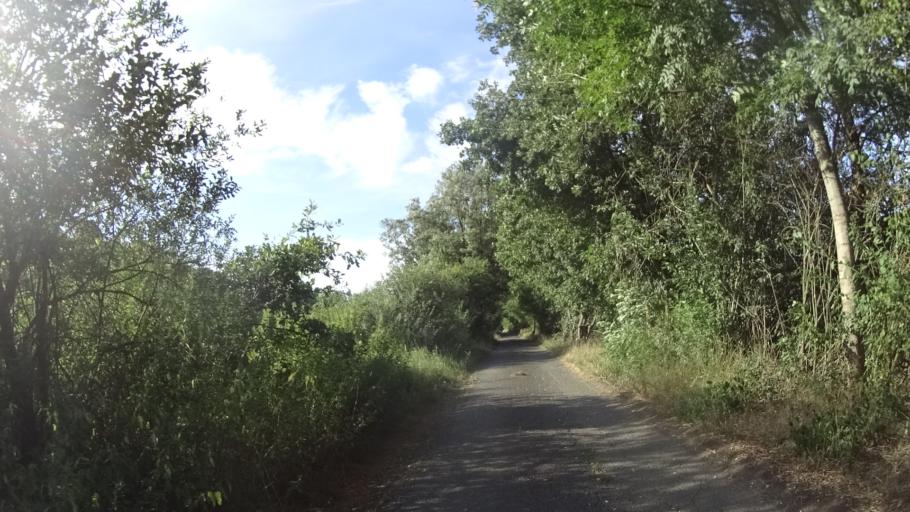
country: AT
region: Lower Austria
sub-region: Politischer Bezirk Mistelbach
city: Rabensburg
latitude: 48.6024
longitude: 16.9492
